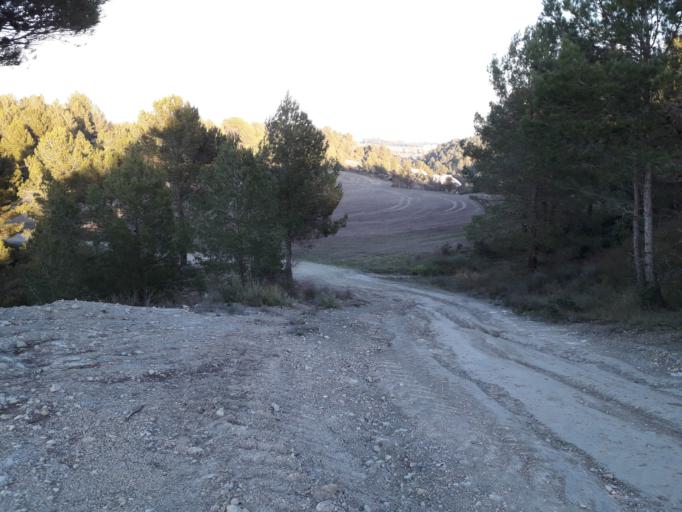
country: ES
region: Catalonia
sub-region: Provincia de Barcelona
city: Jorba
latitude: 41.5796
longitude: 1.5773
